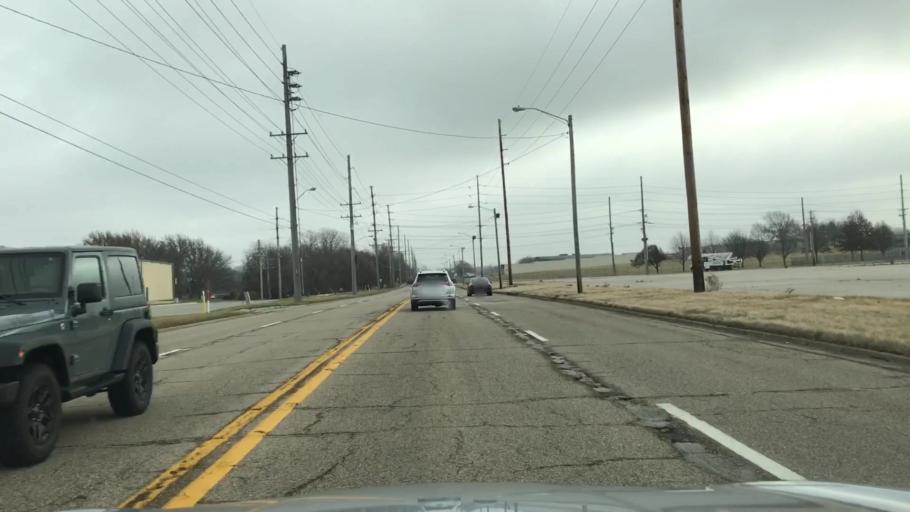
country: US
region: Illinois
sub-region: McLean County
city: Normal
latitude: 40.5027
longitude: -88.9498
